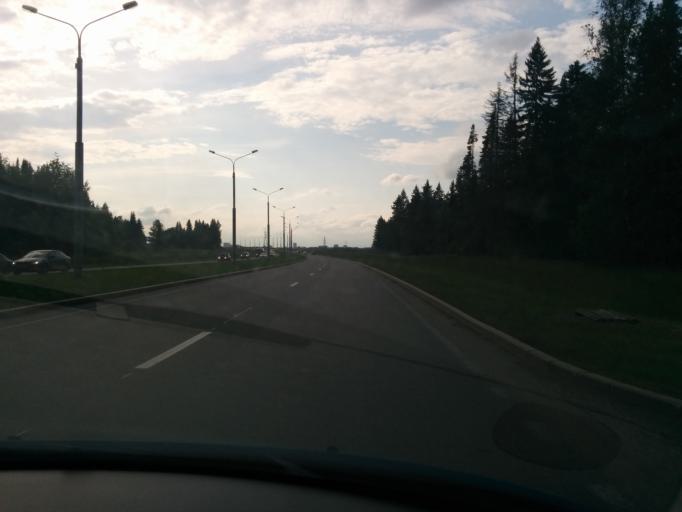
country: RU
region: Perm
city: Ferma
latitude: 58.0034
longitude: 56.3721
